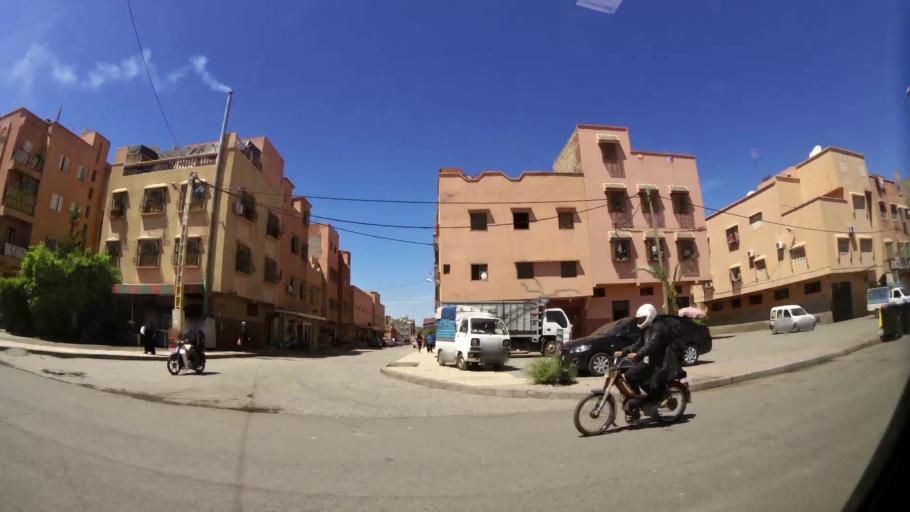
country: MA
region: Marrakech-Tensift-Al Haouz
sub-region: Marrakech
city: Marrakesh
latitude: 31.6555
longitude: -7.9903
